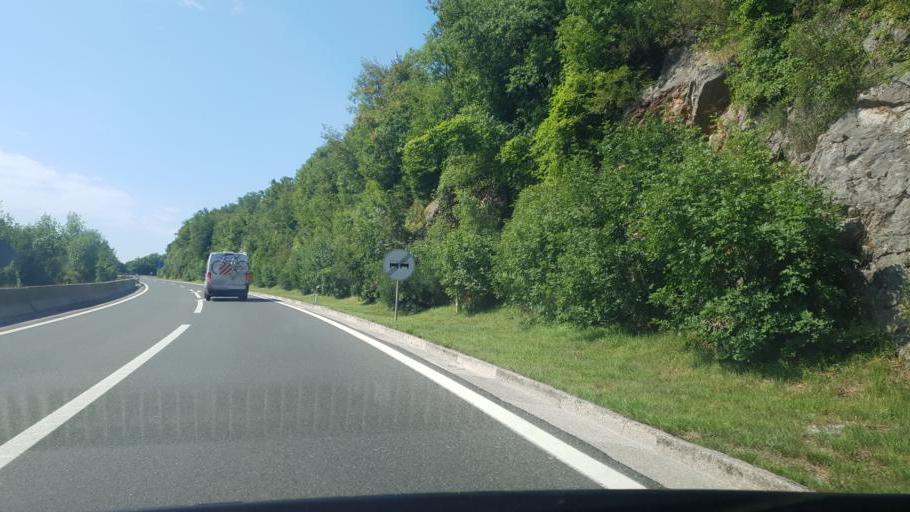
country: HR
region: Primorsko-Goranska
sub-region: Grad Opatija
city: Opatija
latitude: 45.3447
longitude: 14.2989
